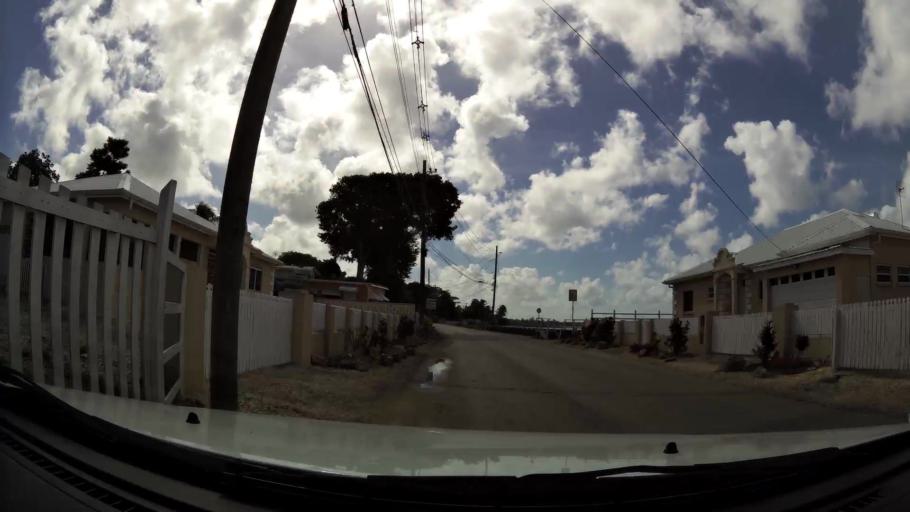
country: BB
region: Saint Lucy
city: Checker Hall
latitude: 13.2706
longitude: -59.6457
